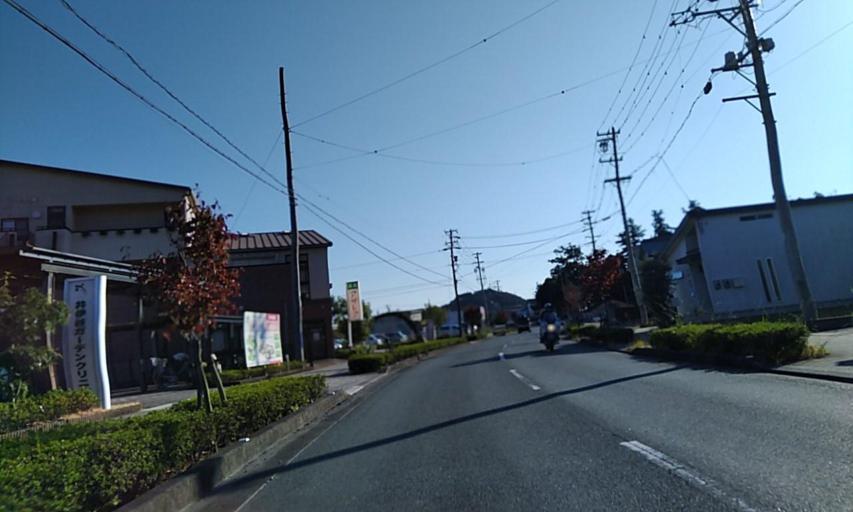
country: JP
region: Shizuoka
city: Hamakita
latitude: 34.8311
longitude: 137.6703
